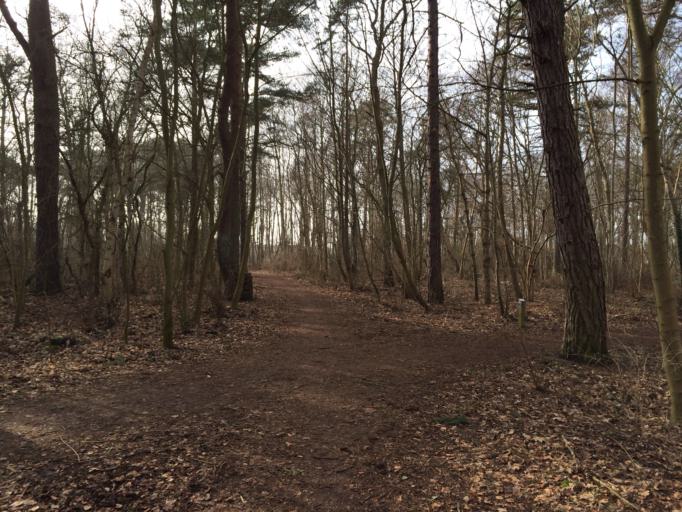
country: SE
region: Skane
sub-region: Vellinge Kommun
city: Skanor med Falsterbo
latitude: 55.3923
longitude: 12.8402
